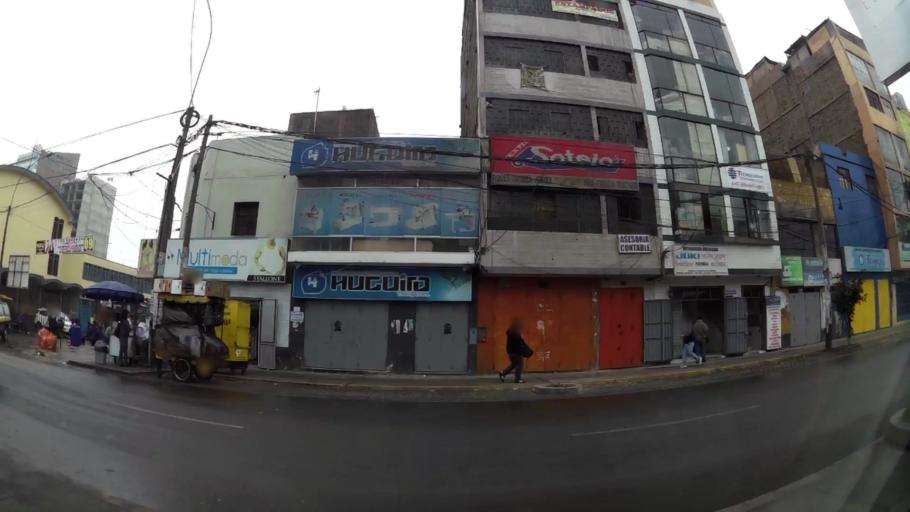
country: PE
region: Lima
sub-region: Lima
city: San Luis
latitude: -12.0651
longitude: -77.0150
